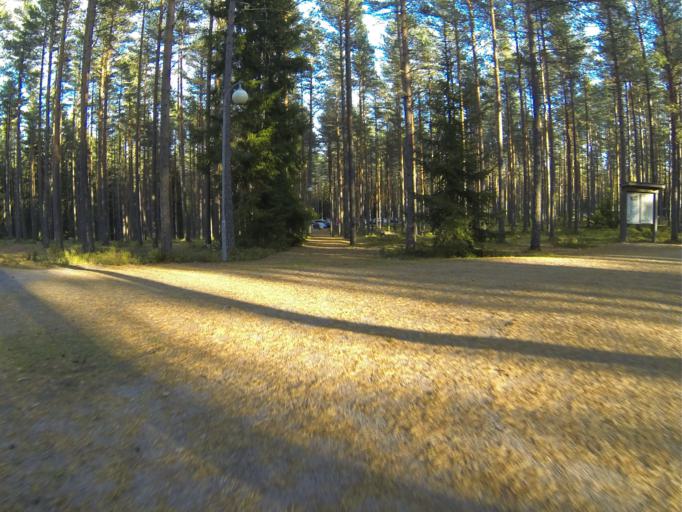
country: FI
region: Varsinais-Suomi
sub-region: Salo
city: Saerkisalo
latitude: 60.2099
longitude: 22.9362
